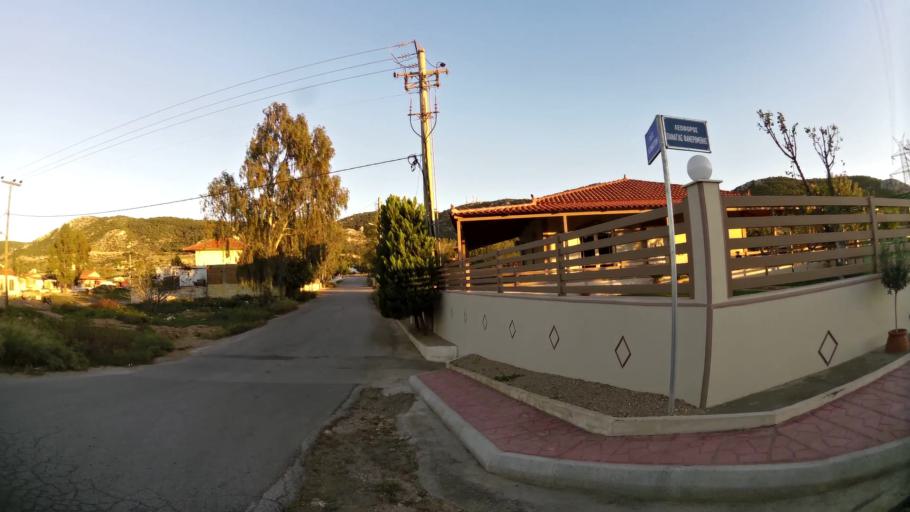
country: GR
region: Attica
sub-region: Nomarchia Athinas
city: Skaramangas
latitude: 38.0388
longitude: 23.6287
